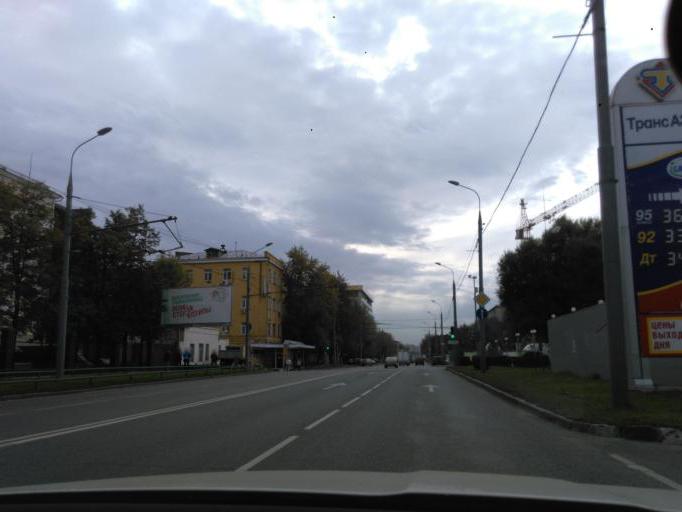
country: RU
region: Moscow
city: Ostankinskiy
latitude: 55.8201
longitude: 37.5920
